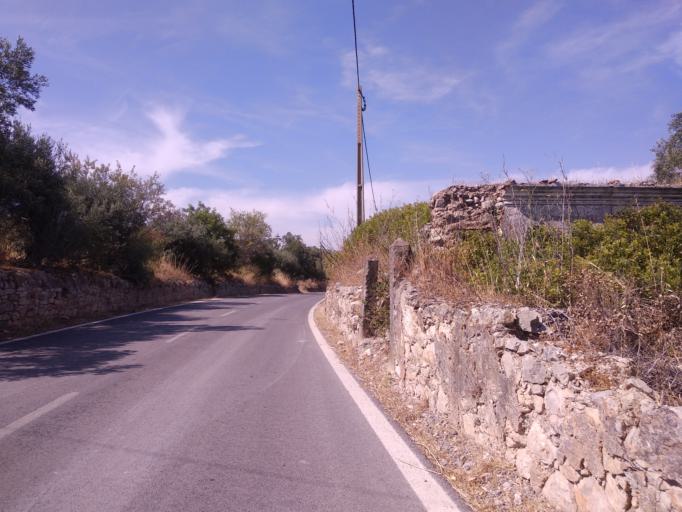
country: PT
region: Faro
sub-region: Faro
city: Santa Barbara de Nexe
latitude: 37.1189
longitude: -7.9580
